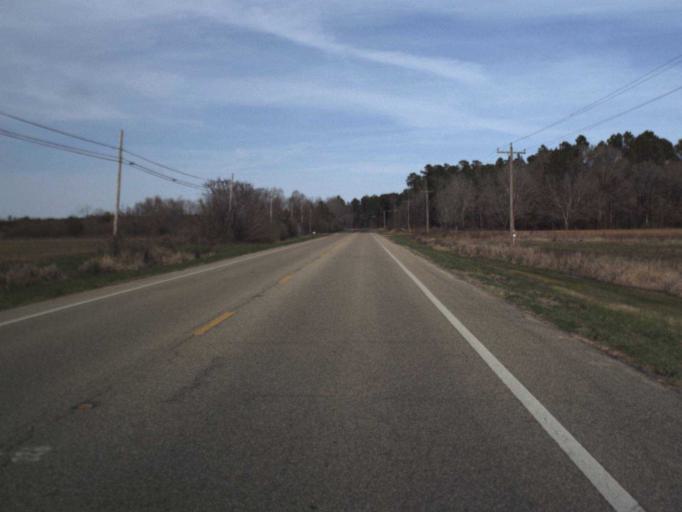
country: US
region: Florida
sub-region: Washington County
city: Chipley
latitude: 30.8423
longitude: -85.5315
